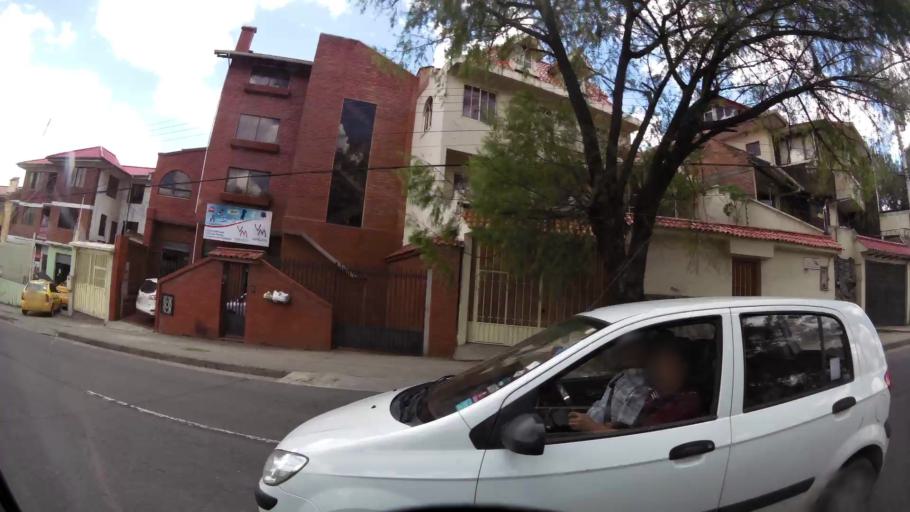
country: EC
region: Azuay
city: Cuenca
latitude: -2.8861
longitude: -78.9948
